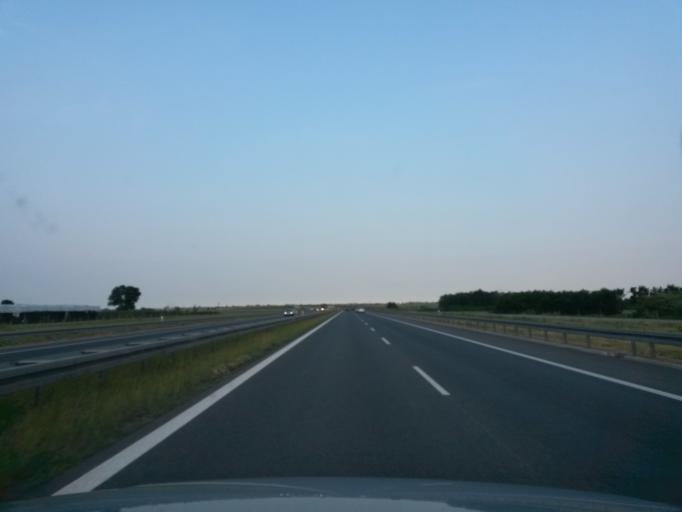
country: PL
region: Lower Silesian Voivodeship
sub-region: Powiat olesnicki
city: Dobroszyce
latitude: 51.2228
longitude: 17.3061
